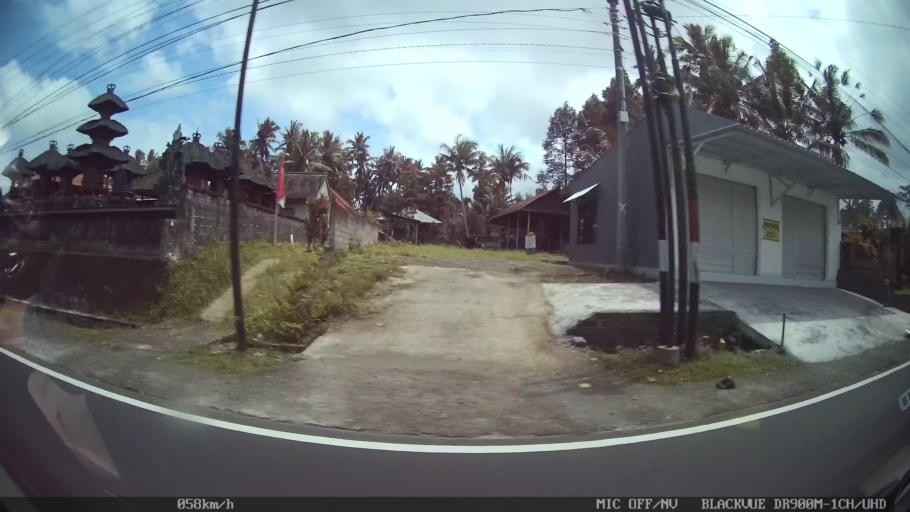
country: ID
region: Bali
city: Banjar Kubu
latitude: -8.4357
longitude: 115.4162
